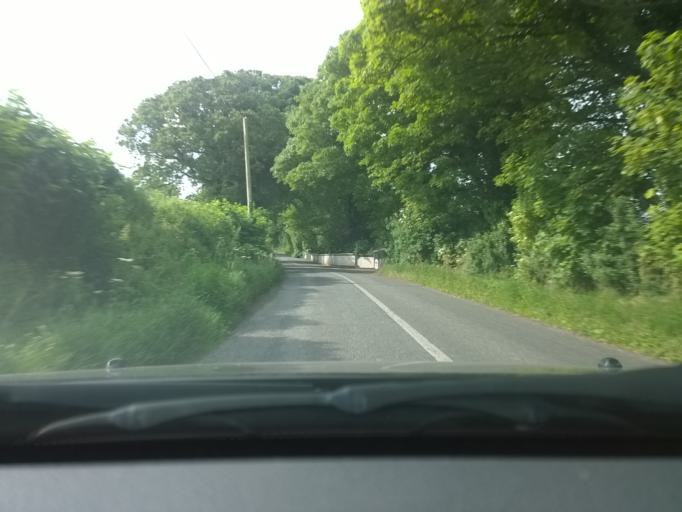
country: IE
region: Leinster
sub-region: Kildare
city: Kildare
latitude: 53.1739
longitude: -6.9142
